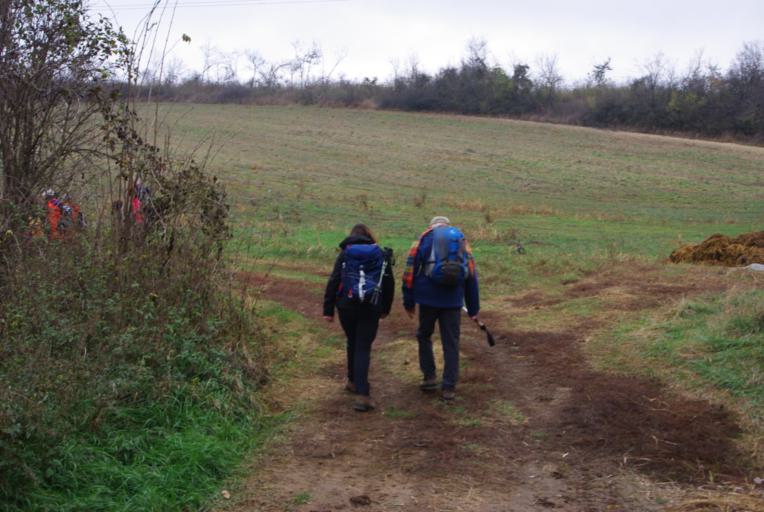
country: HU
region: Pest
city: Isaszeg
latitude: 47.4917
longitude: 19.3861
